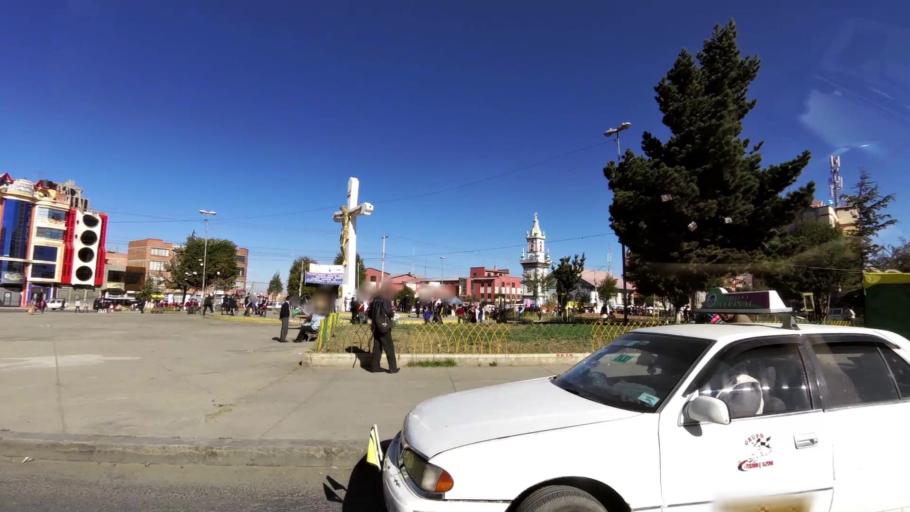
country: BO
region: La Paz
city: La Paz
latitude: -16.5253
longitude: -68.2001
